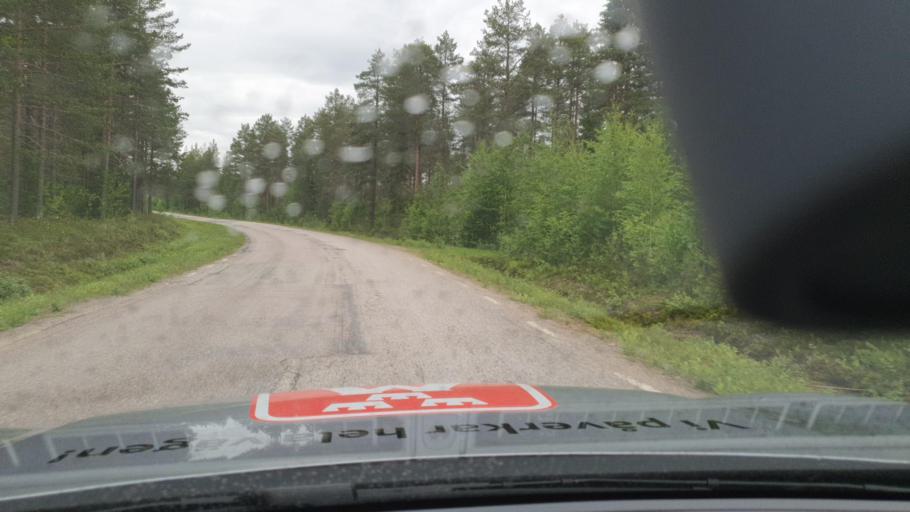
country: SE
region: Norrbotten
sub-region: Overkalix Kommun
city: OEverkalix
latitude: 66.3634
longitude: 22.8039
